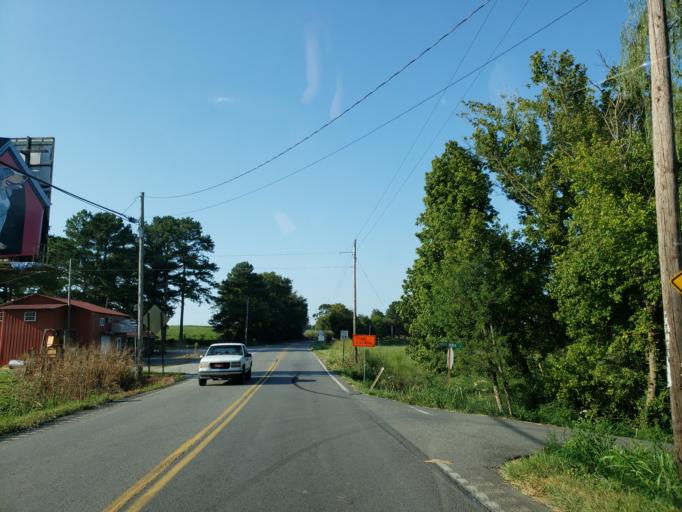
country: US
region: Tennessee
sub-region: Bradley County
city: Wildwood Lake
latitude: 34.9886
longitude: -84.7385
